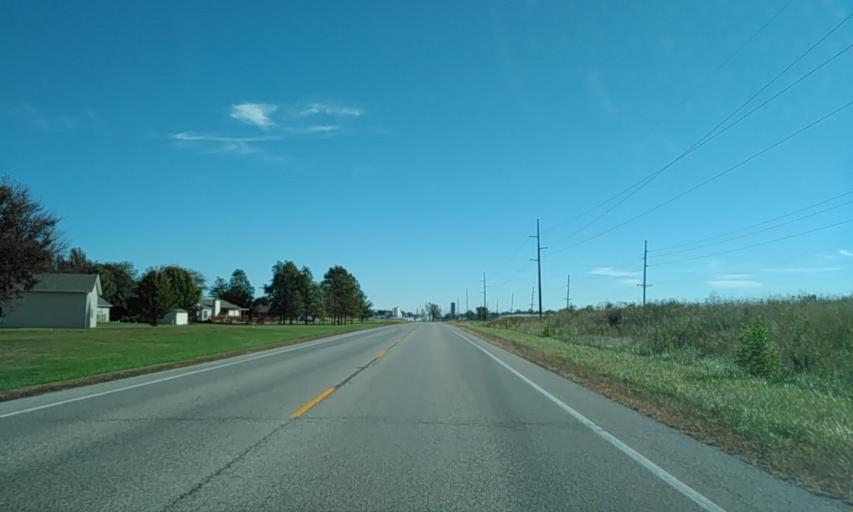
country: US
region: Illinois
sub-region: Madison County
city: Highland
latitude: 38.7369
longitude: -89.7055
